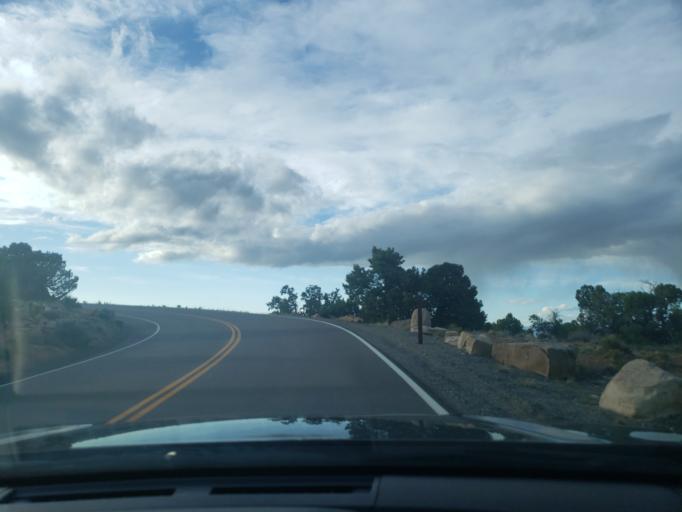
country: US
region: Colorado
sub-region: Mesa County
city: Redlands
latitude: 39.0330
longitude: -108.6495
